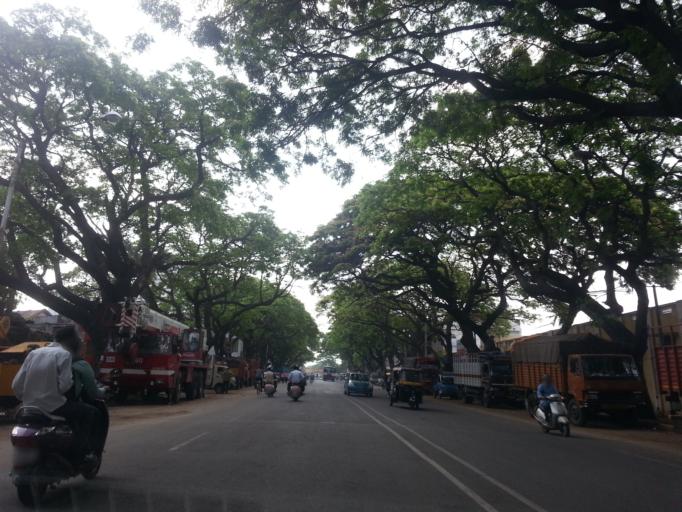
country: IN
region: Karnataka
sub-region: Mysore
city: Mysore
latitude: 12.3226
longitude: 76.6459
